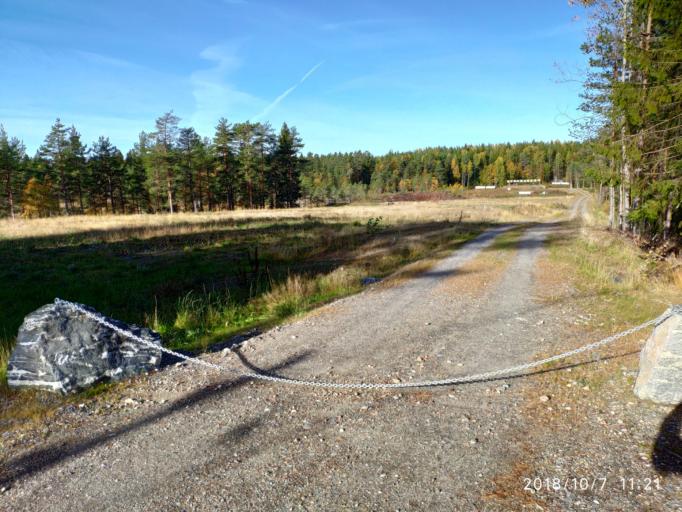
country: NO
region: Akershus
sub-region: Nes
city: Neskollen
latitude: 60.2108
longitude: 11.3198
